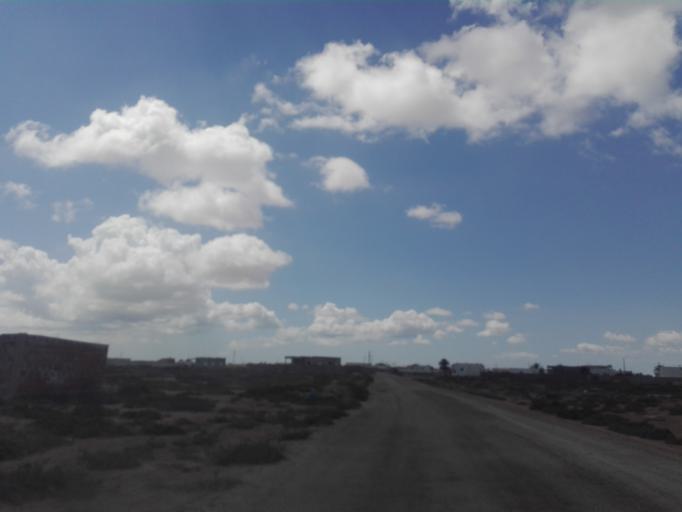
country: TN
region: Safaqis
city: Jabinyanah
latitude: 34.8263
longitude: 11.2541
